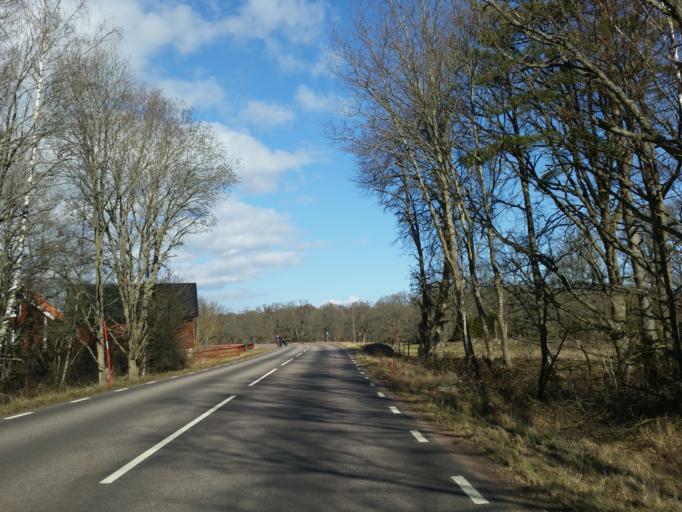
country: SE
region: Kalmar
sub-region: Monsteras Kommun
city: Timmernabben
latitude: 56.9185
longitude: 16.4231
